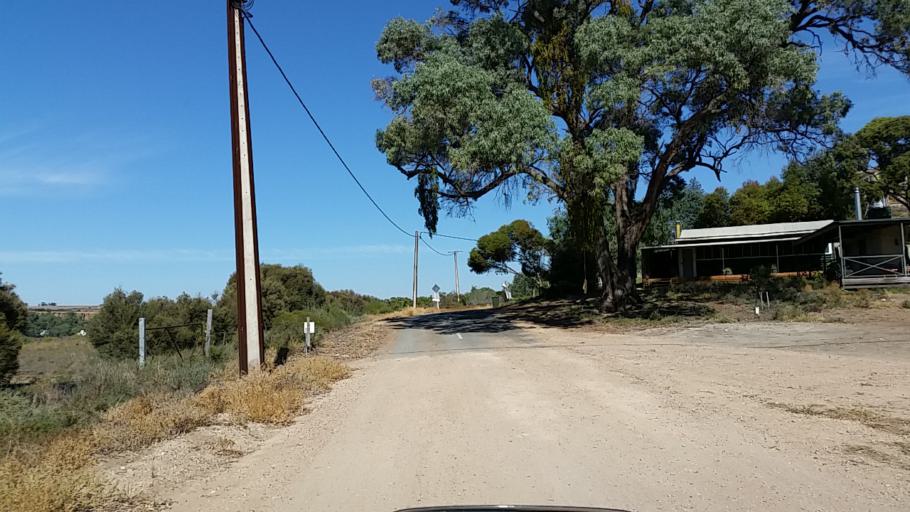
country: AU
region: South Australia
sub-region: Mid Murray
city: Mannum
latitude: -34.7013
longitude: 139.5731
